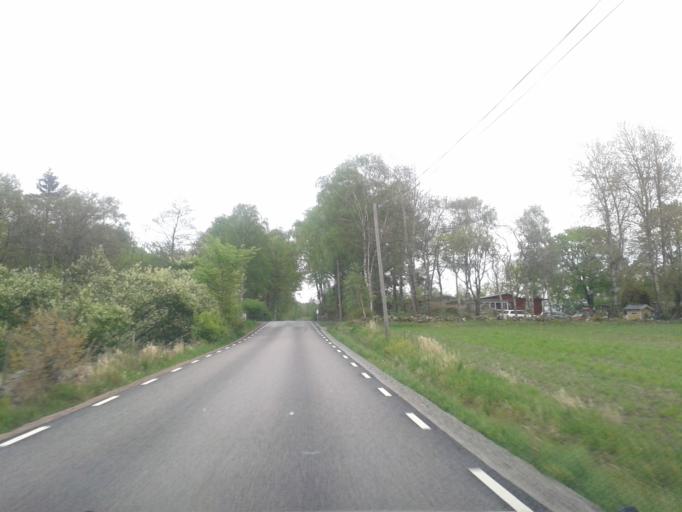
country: SE
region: Vaestra Goetaland
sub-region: Kungalvs Kommun
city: Kode
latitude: 57.9104
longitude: 11.8789
